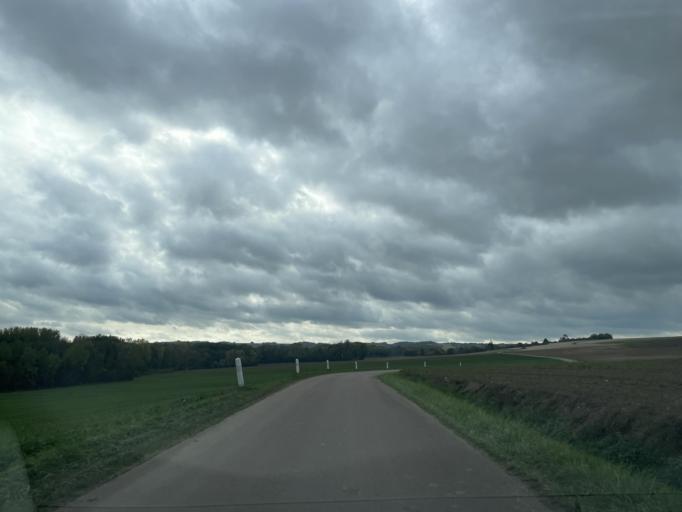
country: FR
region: Bourgogne
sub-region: Departement de l'Yonne
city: Aillant-sur-Tholon
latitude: 47.8314
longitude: 3.3558
